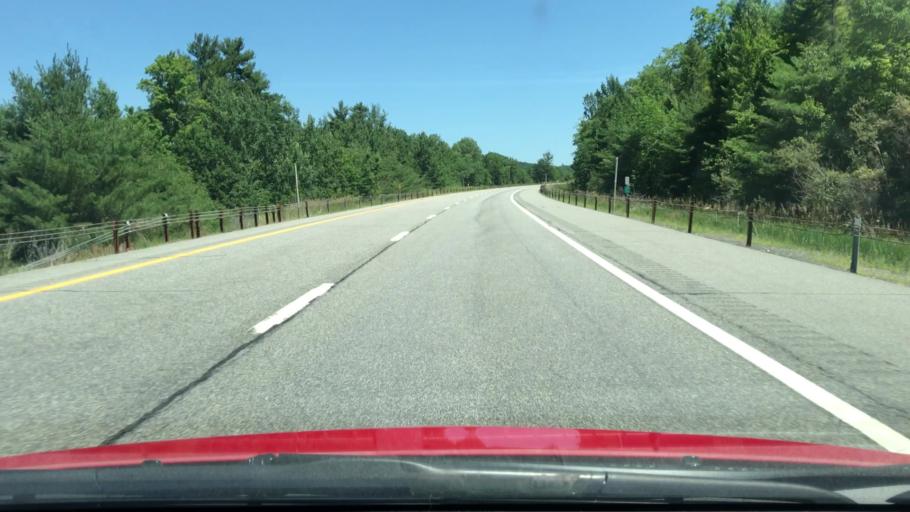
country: US
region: New York
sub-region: Essex County
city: Elizabethtown
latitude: 44.1758
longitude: -73.5806
